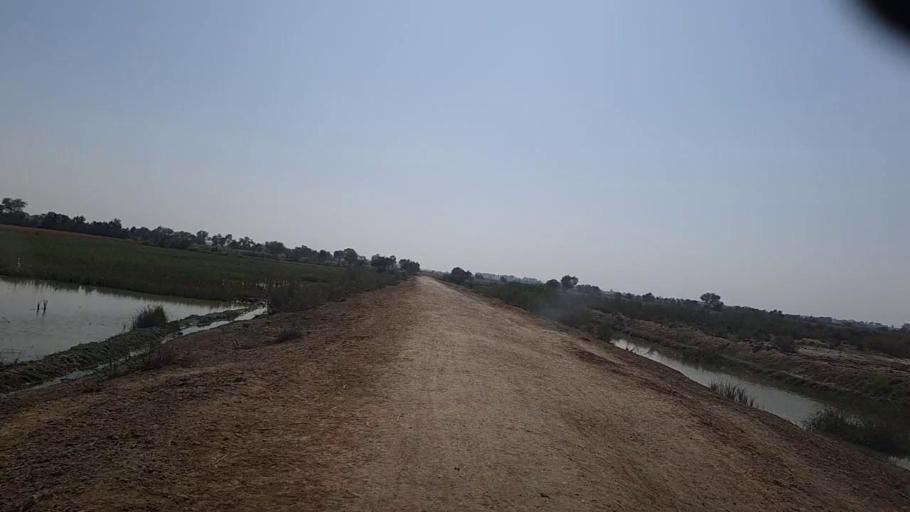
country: PK
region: Sindh
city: Thul
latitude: 28.1688
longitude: 68.7668
